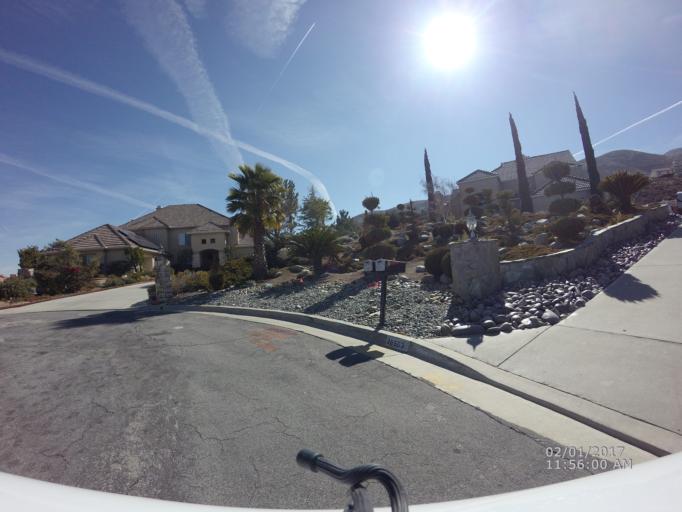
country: US
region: California
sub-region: Los Angeles County
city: Palmdale
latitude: 34.5439
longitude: -118.1356
